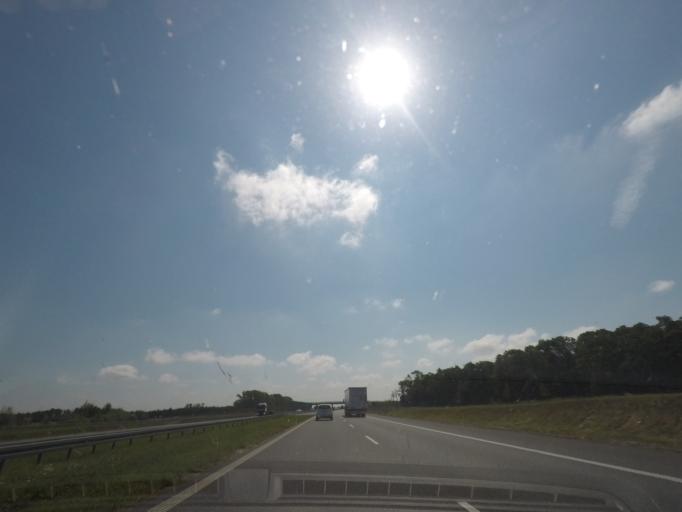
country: PL
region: Kujawsko-Pomorskie
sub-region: Powiat wloclawski
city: Kowal
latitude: 52.4825
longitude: 19.1634
